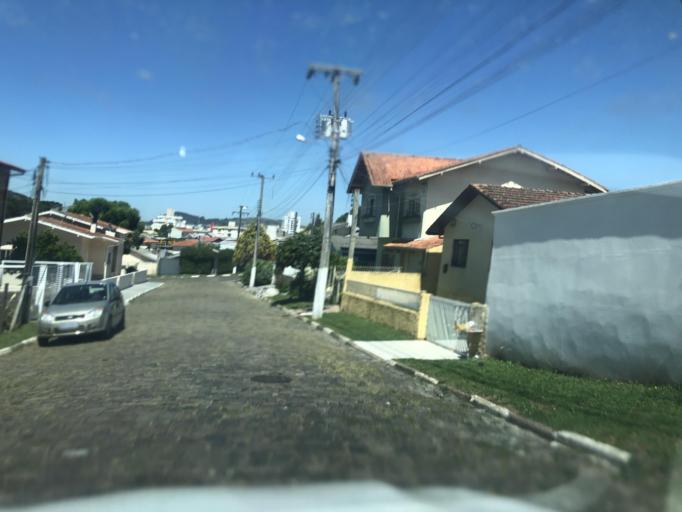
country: BR
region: Santa Catarina
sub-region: Lages
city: Lages
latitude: -27.8212
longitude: -50.3105
